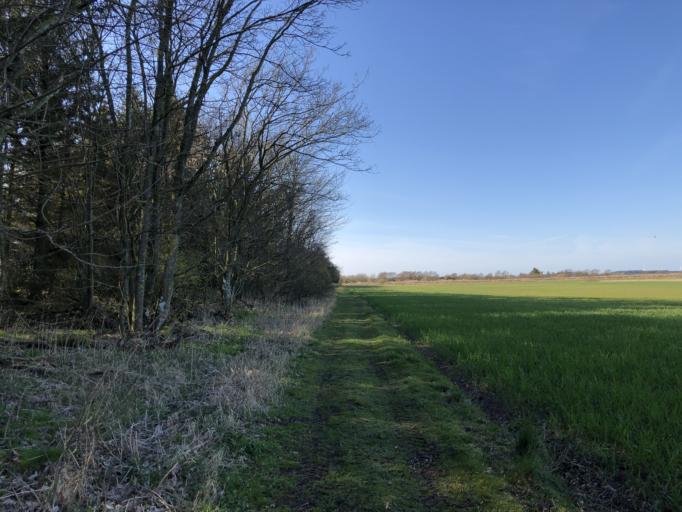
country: DK
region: Central Jutland
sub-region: Holstebro Kommune
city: Ulfborg
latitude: 56.3282
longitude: 8.3165
